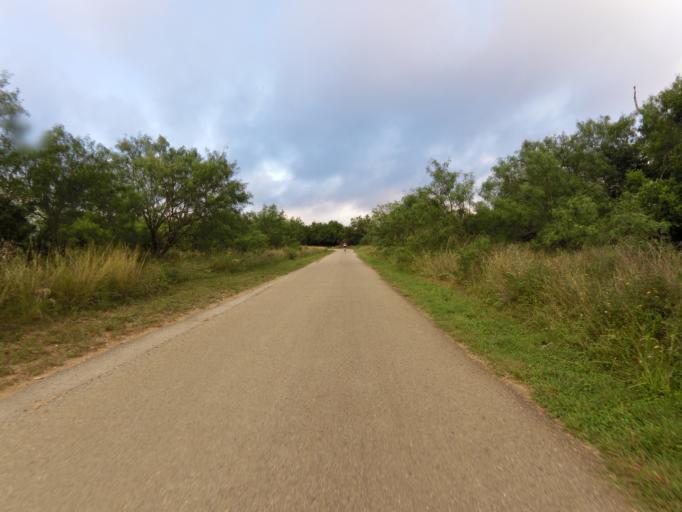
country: US
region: Texas
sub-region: Bexar County
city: Helotes
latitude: 29.5676
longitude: -98.6225
